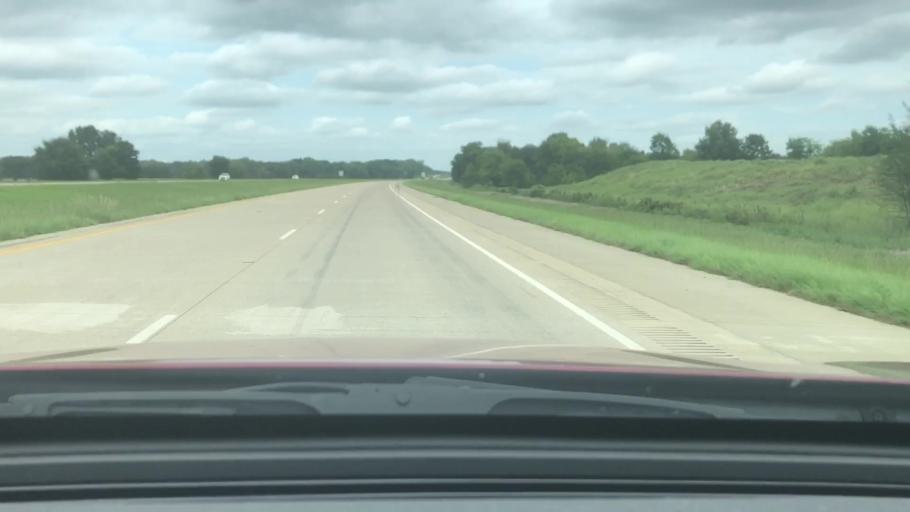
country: US
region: Louisiana
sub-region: Caddo Parish
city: Oil City
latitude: 32.7770
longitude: -93.8895
